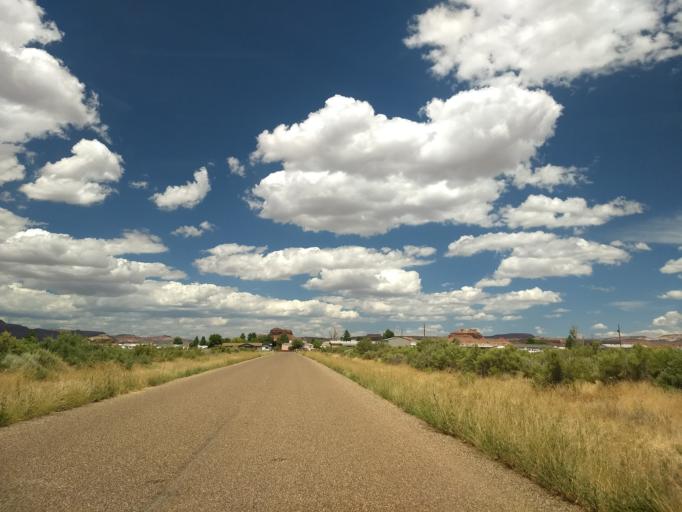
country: US
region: Arizona
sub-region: Coconino County
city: Fredonia
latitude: 36.9574
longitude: -112.5242
